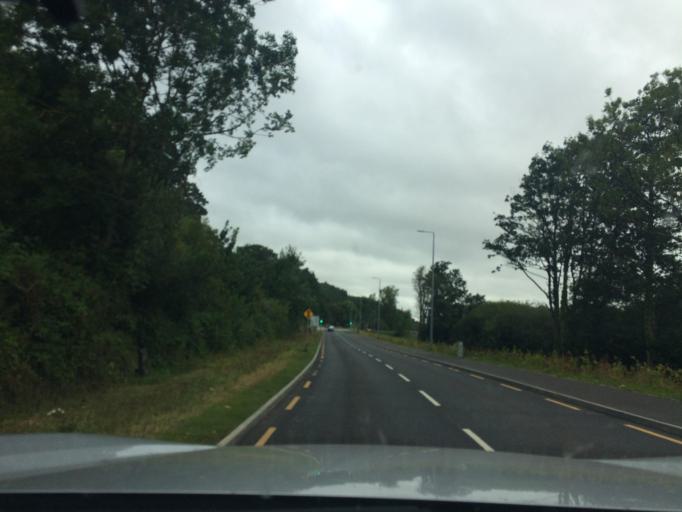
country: IE
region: Munster
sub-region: South Tipperary
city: Cluain Meala
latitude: 52.3450
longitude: -7.7217
